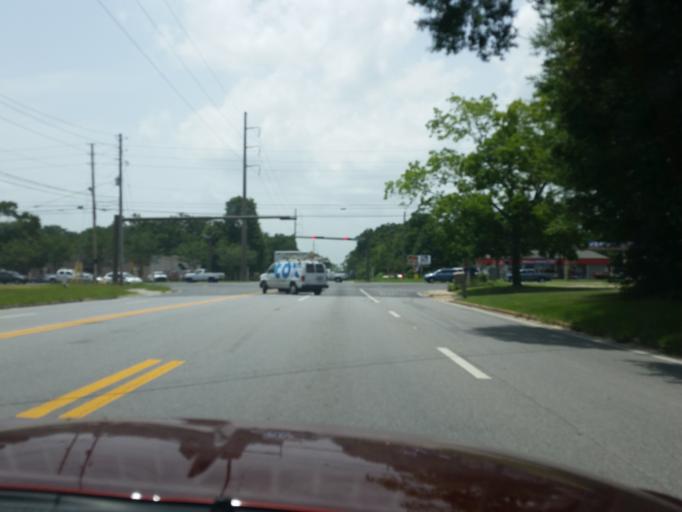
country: US
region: Florida
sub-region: Escambia County
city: Ferry Pass
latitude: 30.5295
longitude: -87.2075
